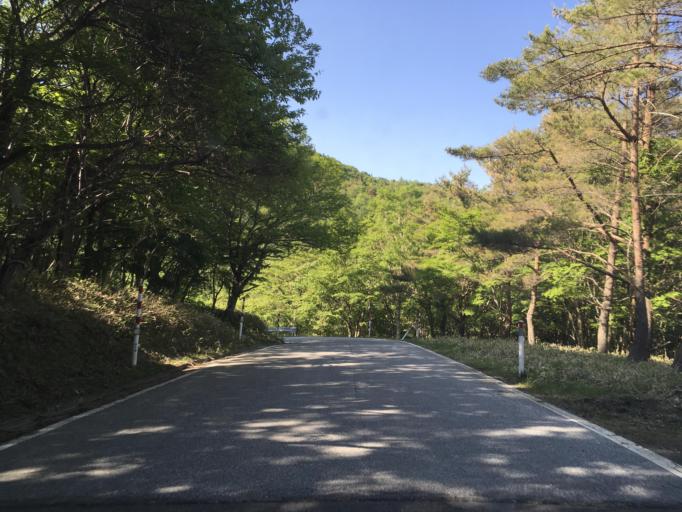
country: JP
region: Iwate
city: Ofunato
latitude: 39.1840
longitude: 141.7462
